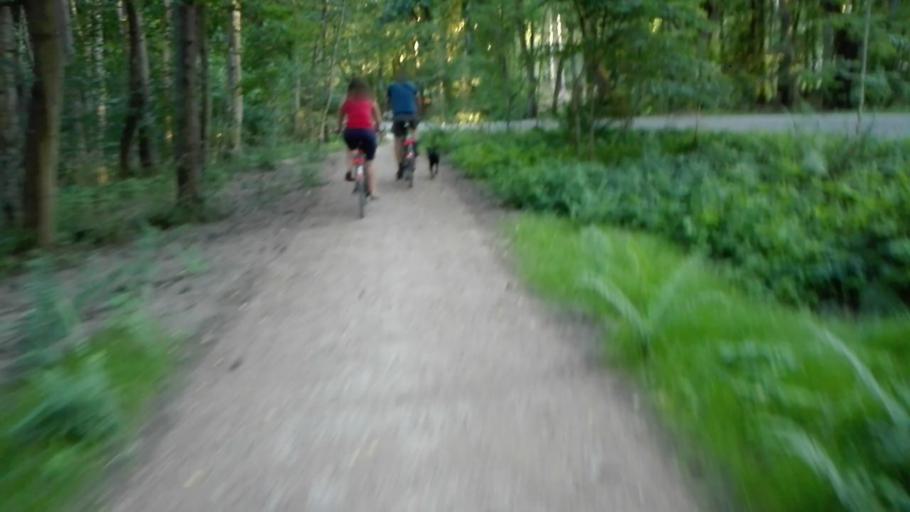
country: PL
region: West Pomeranian Voivodeship
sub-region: Powiat policki
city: Dobra
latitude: 53.4689
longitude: 14.3625
